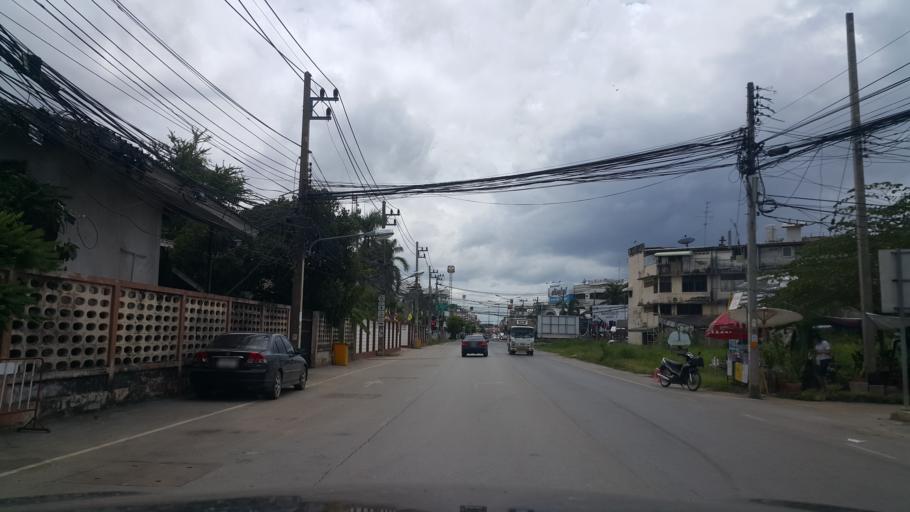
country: TH
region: Sukhothai
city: Sukhothai
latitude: 17.0066
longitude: 99.8260
